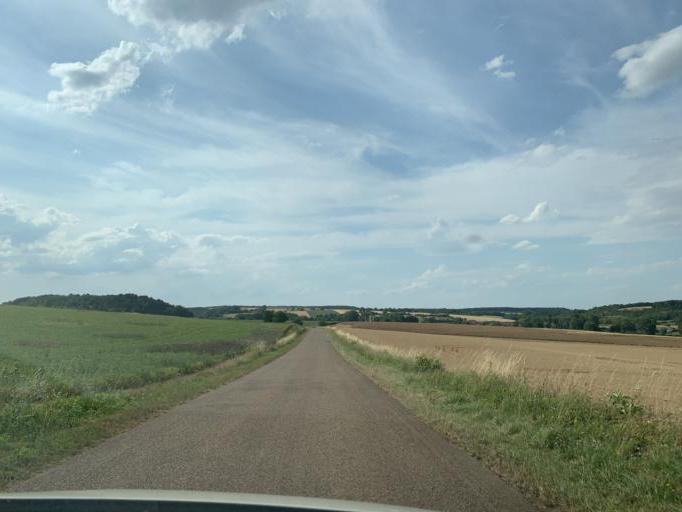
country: FR
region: Bourgogne
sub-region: Departement de l'Yonne
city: Fontenailles
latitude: 47.4715
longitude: 3.4261
